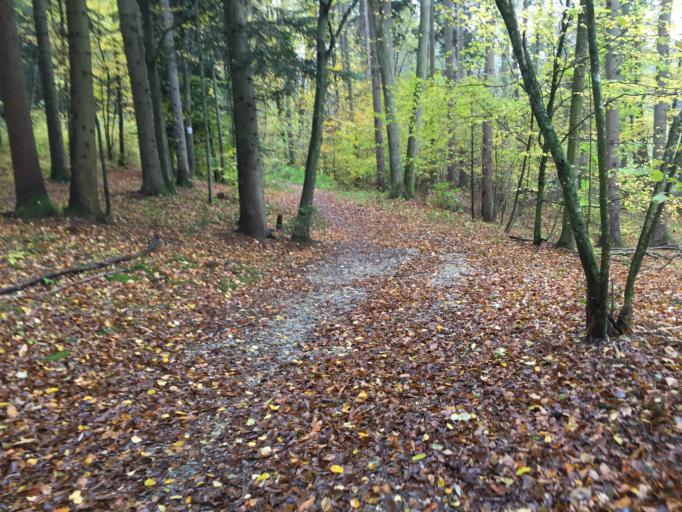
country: AT
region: Styria
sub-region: Politischer Bezirk Graz-Umgebung
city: Hart bei Graz
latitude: 47.0708
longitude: 15.5433
